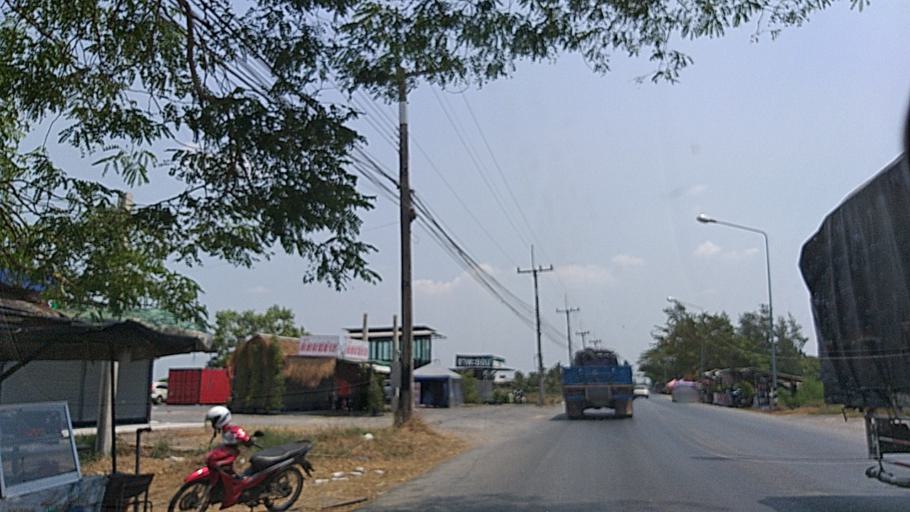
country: TH
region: Chachoengsao
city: Bang Nam Priao
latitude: 13.9716
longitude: 100.9634
